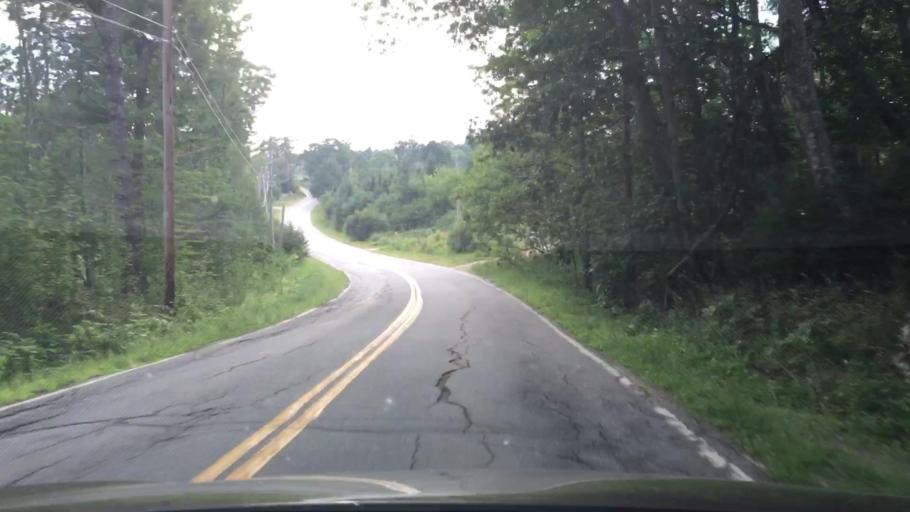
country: US
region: Maine
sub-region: Hancock County
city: Penobscot
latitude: 44.4723
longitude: -68.7319
